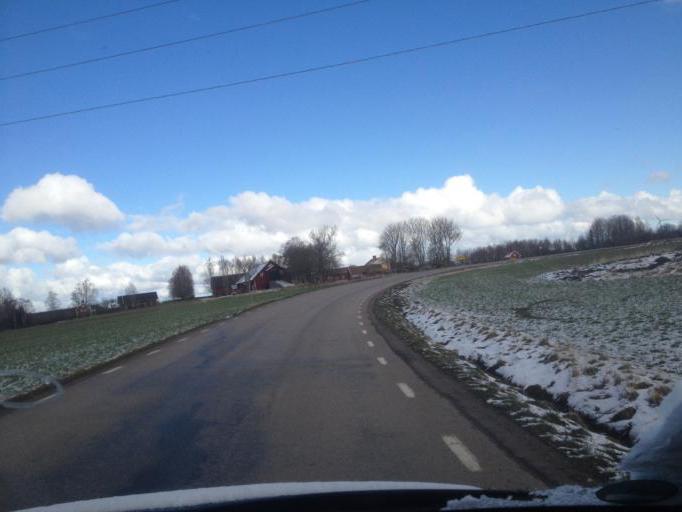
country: SE
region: OEstergoetland
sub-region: Mjolby Kommun
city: Mantorp
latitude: 58.4113
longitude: 15.3037
